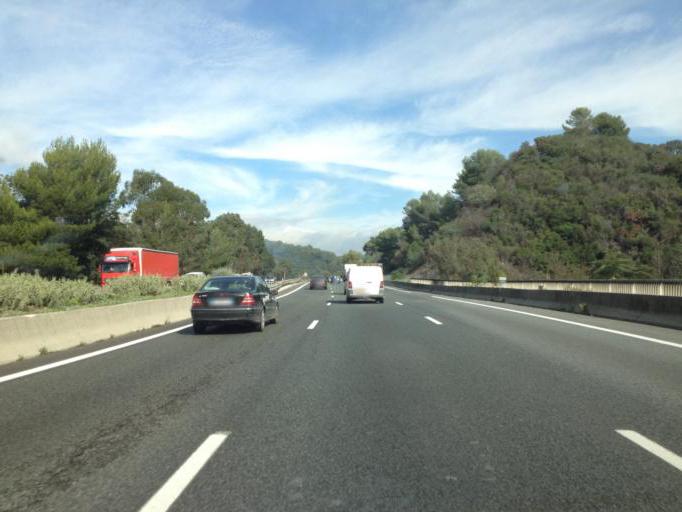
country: FR
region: Provence-Alpes-Cote d'Azur
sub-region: Departement des Alpes-Maritimes
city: La Roquette-sur-Siagne
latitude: 43.5649
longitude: 6.9732
